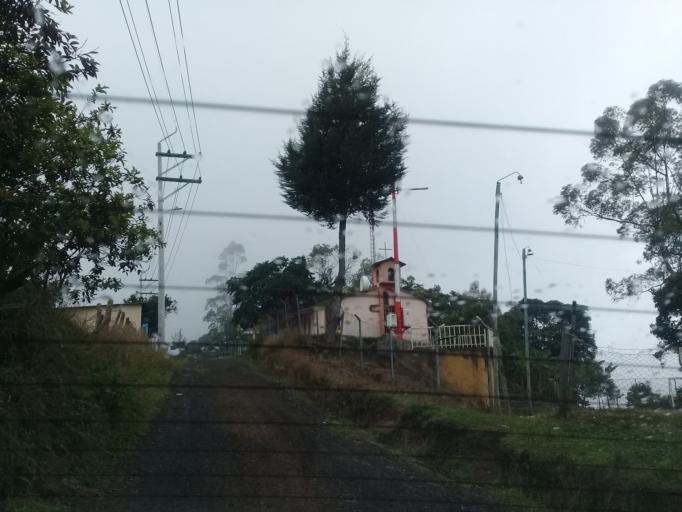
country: CO
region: Cundinamarca
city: Viani
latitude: 4.8323
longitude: -74.5538
